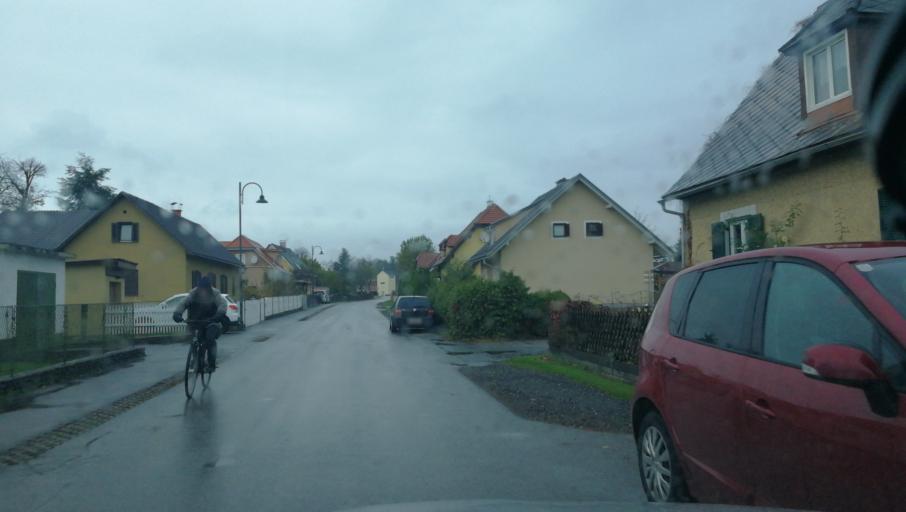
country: AT
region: Styria
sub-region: Politischer Bezirk Leibnitz
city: Strass in Steiermark
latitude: 46.7238
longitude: 15.6318
